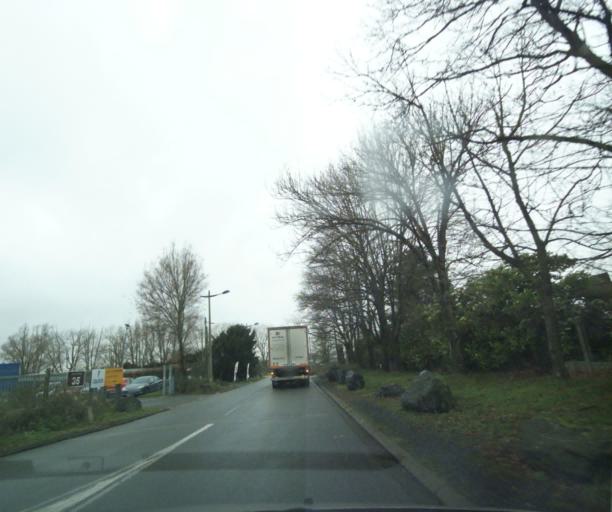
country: FR
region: Nord-Pas-de-Calais
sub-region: Departement du Nord
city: Herin
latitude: 50.3367
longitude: 3.4610
